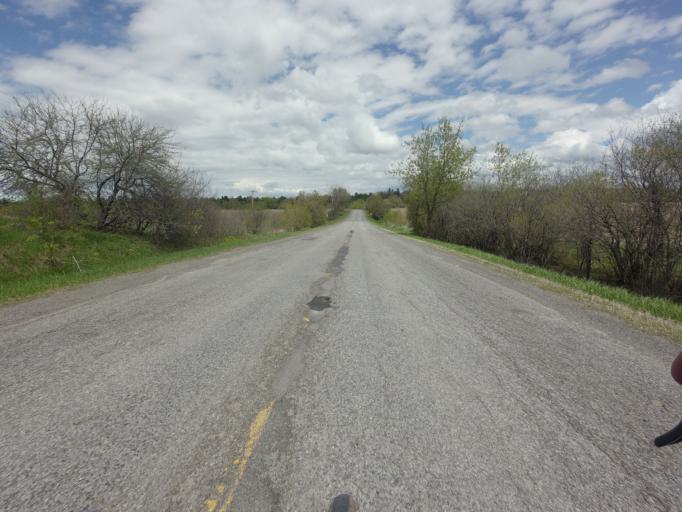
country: CA
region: Ontario
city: Carleton Place
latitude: 45.2642
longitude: -76.2533
